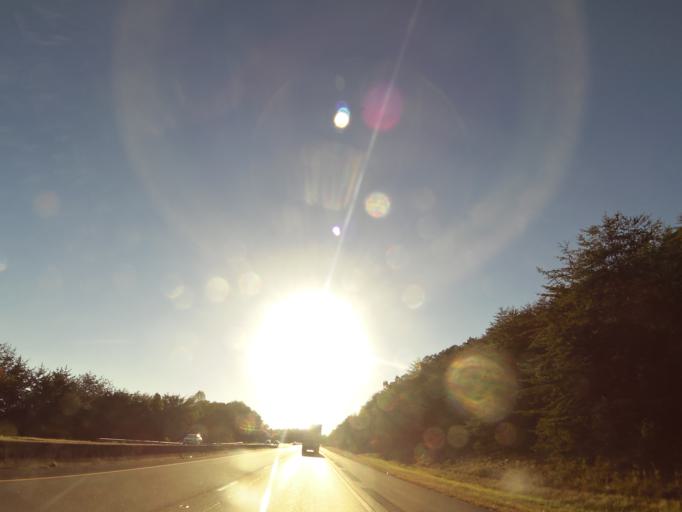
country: US
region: Tennessee
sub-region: Grainger County
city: Bean Station
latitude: 36.3565
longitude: -83.3642
